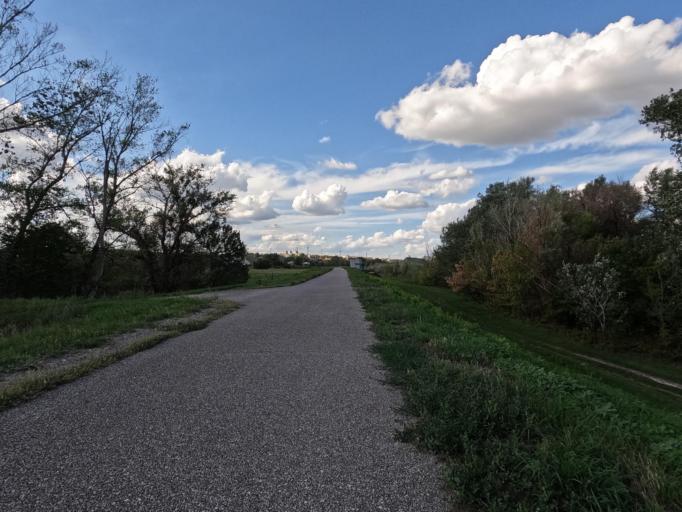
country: HU
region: Tolna
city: Paks
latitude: 46.5984
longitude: 18.8570
